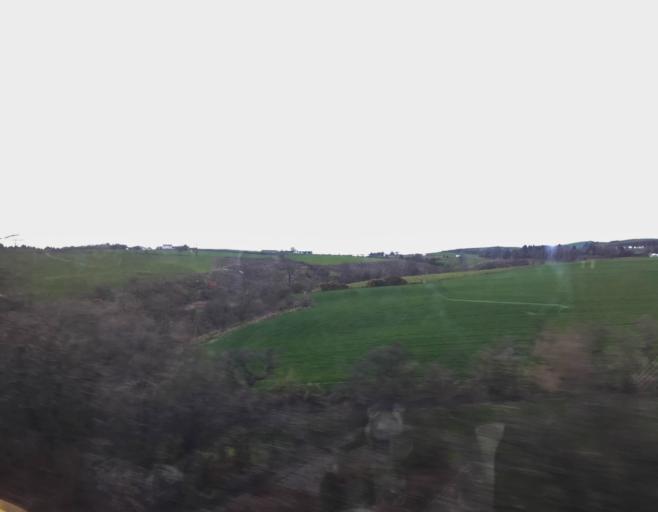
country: GB
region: Scotland
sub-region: Dumfries and Galloway
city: Lockerbie
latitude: 55.0657
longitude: -3.2952
